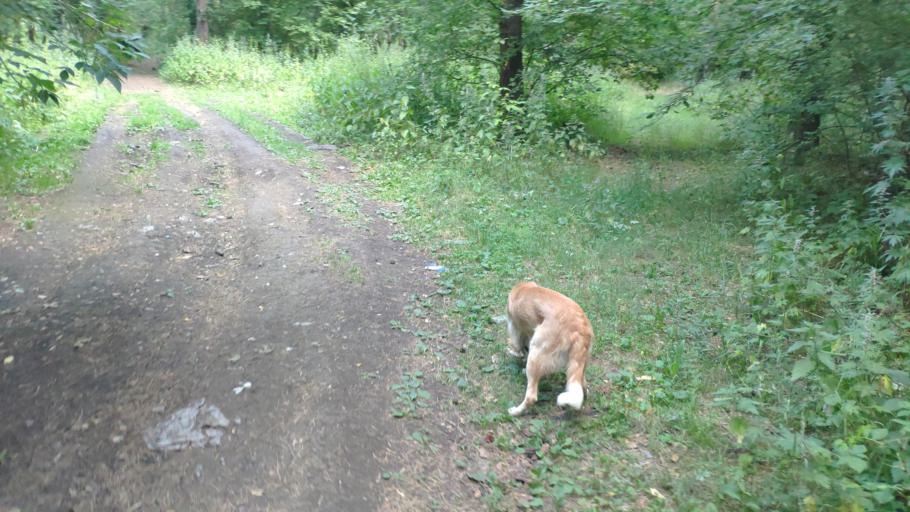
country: RU
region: Bashkortostan
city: Abzakovo
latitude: 53.8087
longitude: 58.6399
